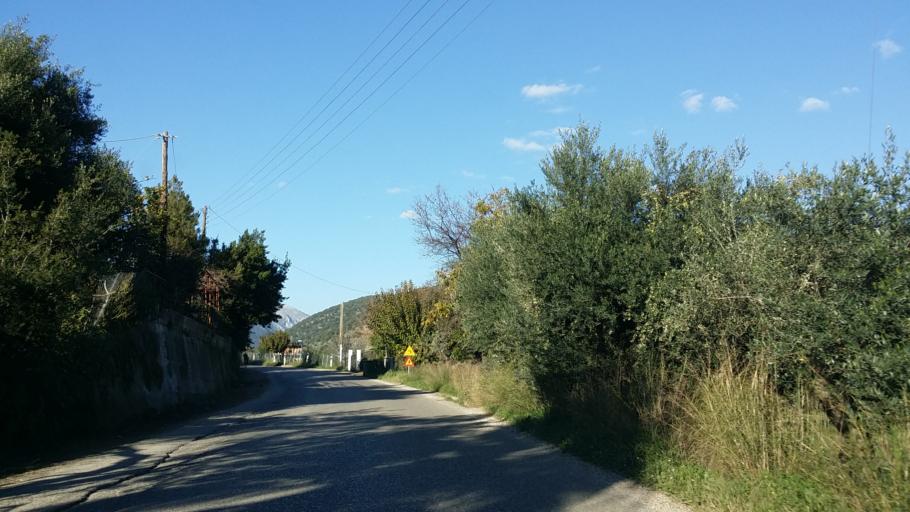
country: GR
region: West Greece
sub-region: Nomos Aitolias kai Akarnanias
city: Astakos
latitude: 38.5693
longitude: 21.0950
